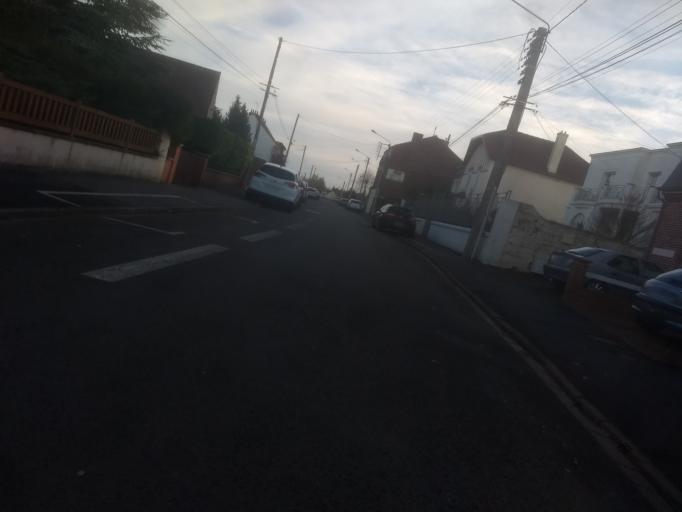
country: FR
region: Nord-Pas-de-Calais
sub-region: Departement du Pas-de-Calais
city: Arras
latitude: 50.2794
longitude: 2.7864
